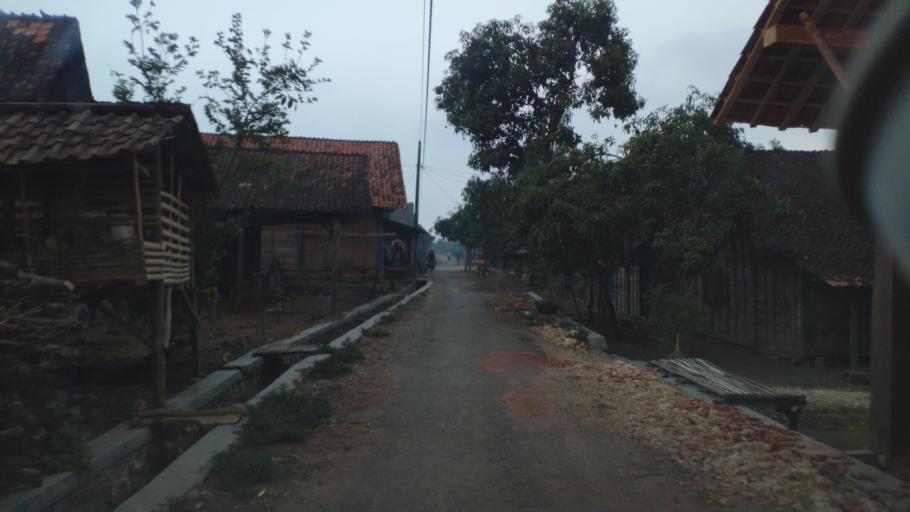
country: ID
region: Central Java
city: Temanjang
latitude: -7.1140
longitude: 111.3931
